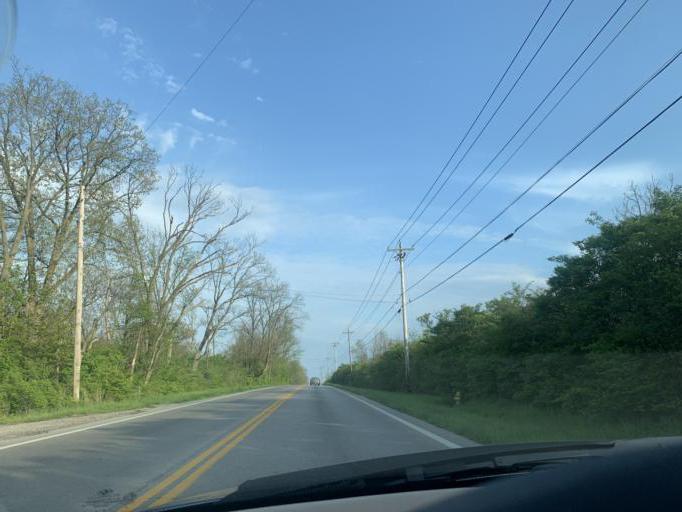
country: US
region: Ohio
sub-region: Hamilton County
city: Glendale
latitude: 39.2698
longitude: -84.4742
